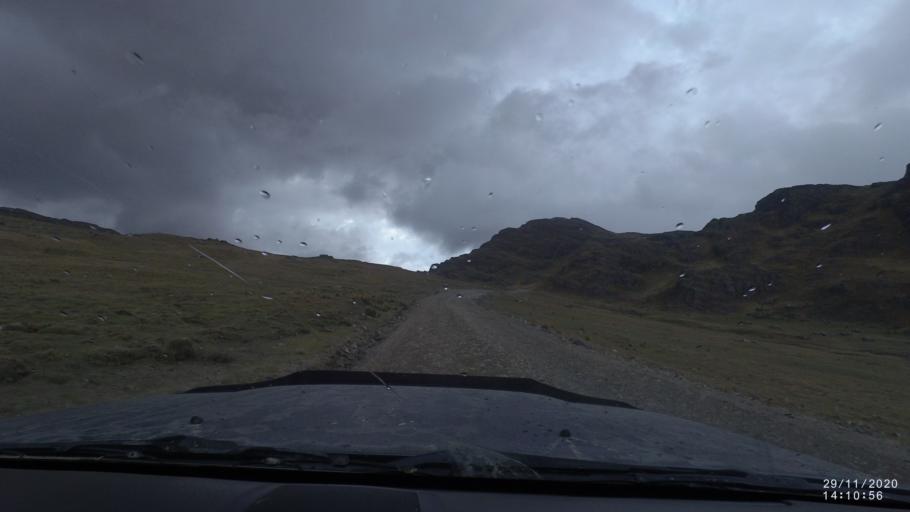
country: BO
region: Cochabamba
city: Sipe Sipe
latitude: -17.2320
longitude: -66.3906
